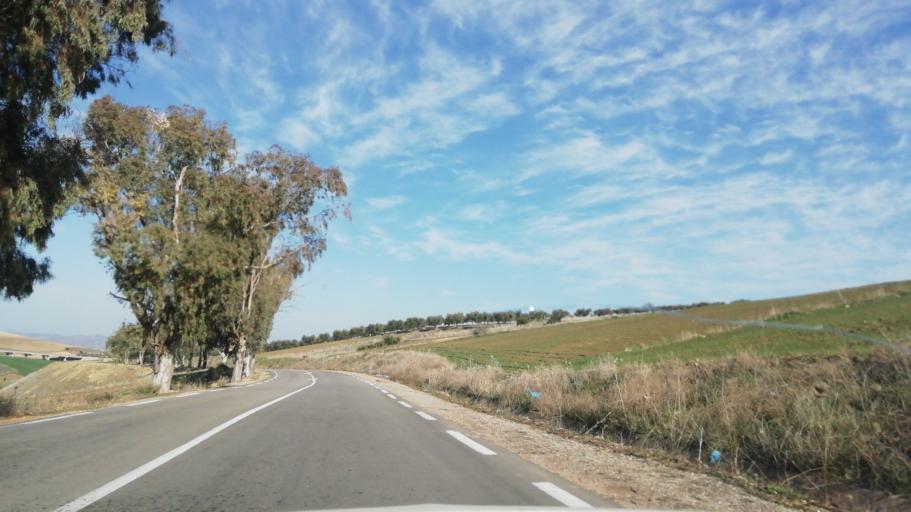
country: DZ
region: Tlemcen
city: Chetouane
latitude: 34.9665
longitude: -1.2468
